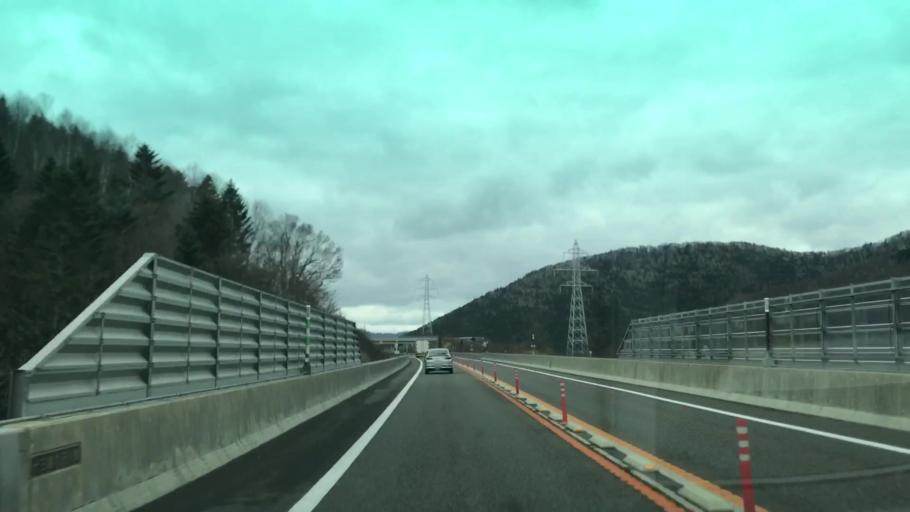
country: JP
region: Hokkaido
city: Shimo-furano
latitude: 43.0539
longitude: 142.6101
